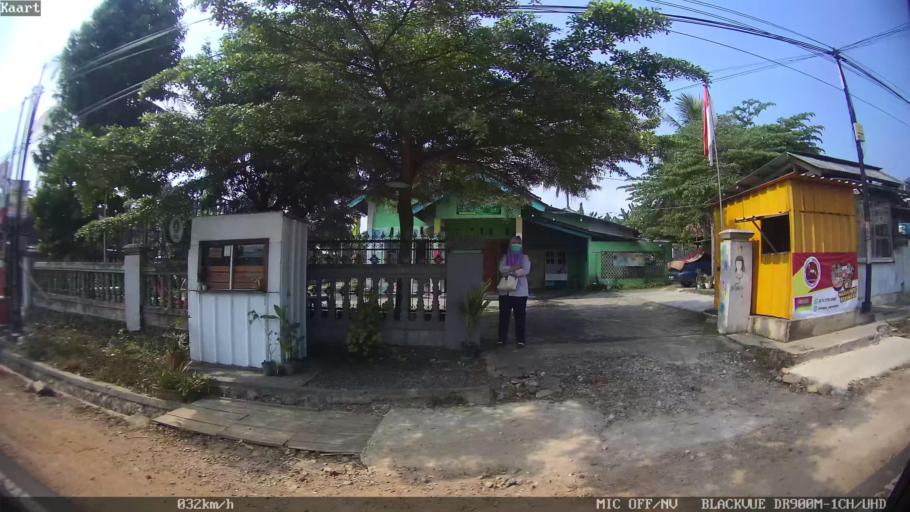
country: ID
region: Lampung
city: Gedongtataan
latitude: -5.3660
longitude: 105.1503
